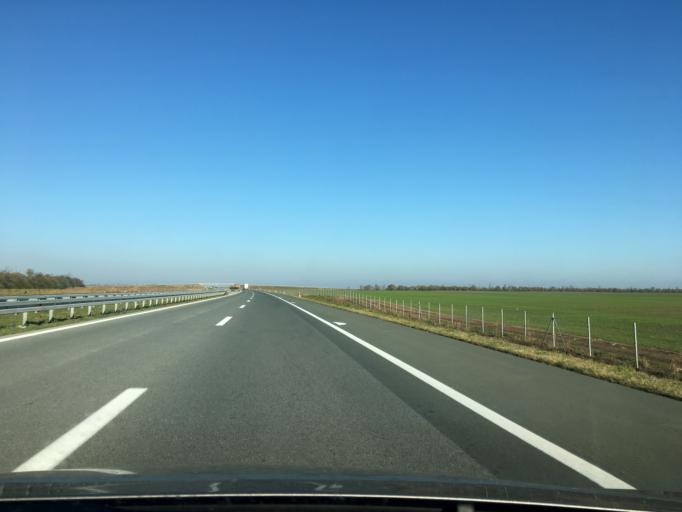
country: RS
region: Autonomna Pokrajina Vojvodina
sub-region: Severnobacki Okrug
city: Mali Igos
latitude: 45.6884
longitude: 19.7266
